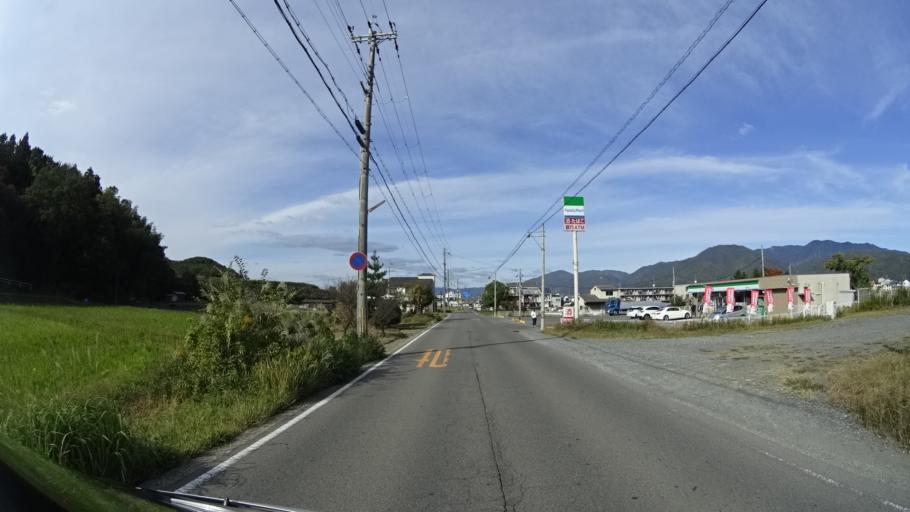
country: JP
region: Kyoto
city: Kameoka
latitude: 35.0037
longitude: 135.5781
